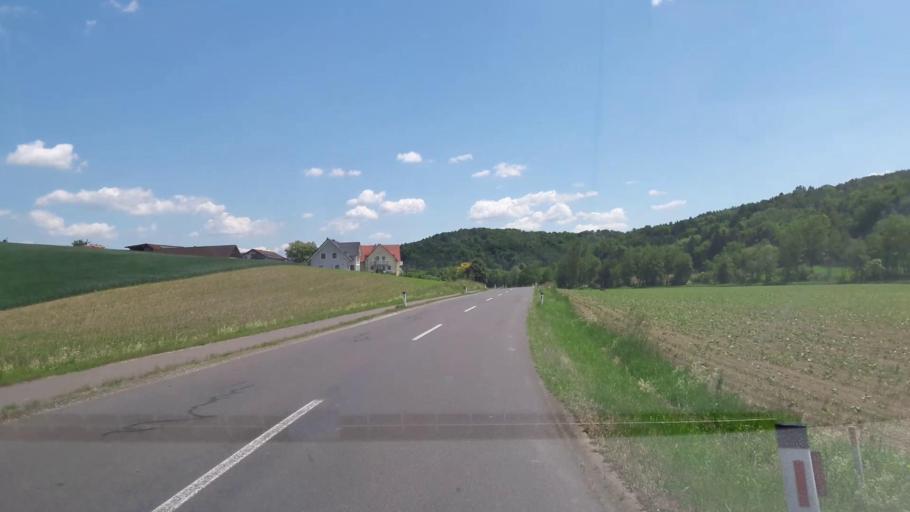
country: AT
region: Styria
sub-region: Politischer Bezirk Suedoststeiermark
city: Unterlamm
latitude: 46.9640
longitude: 16.0913
